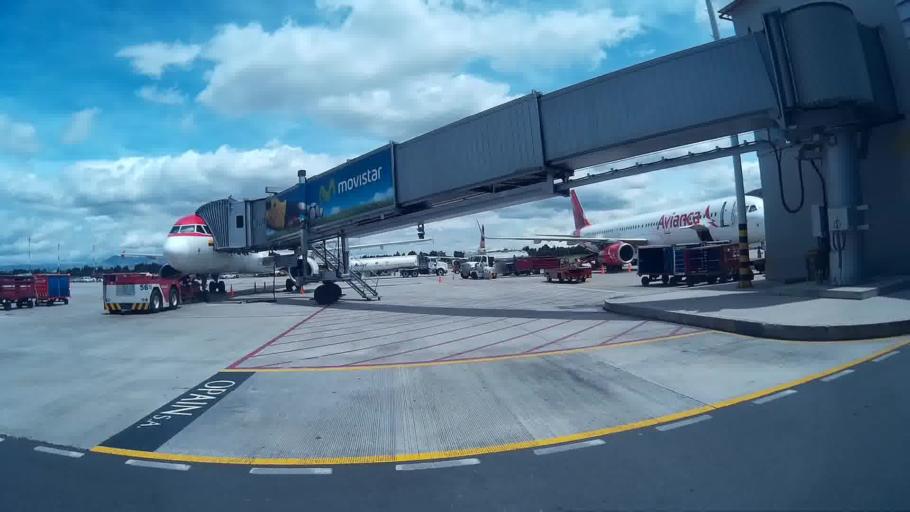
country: CO
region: Cundinamarca
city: Funza
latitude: 4.6983
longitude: -74.1452
